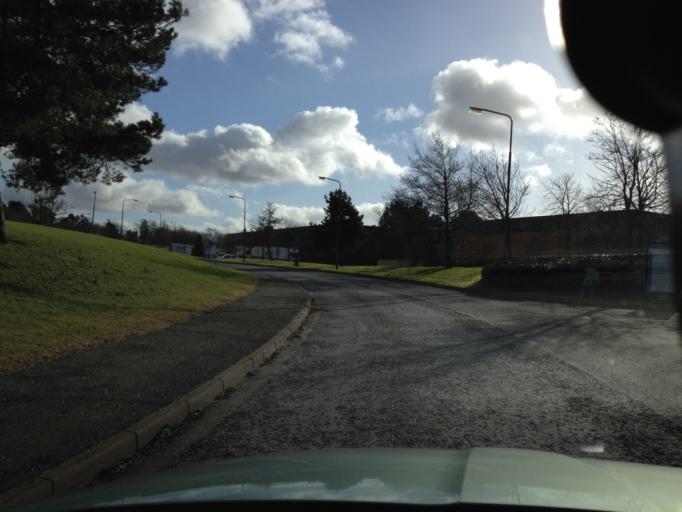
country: GB
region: Scotland
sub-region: West Lothian
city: West Calder
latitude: 55.8649
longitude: -3.5339
